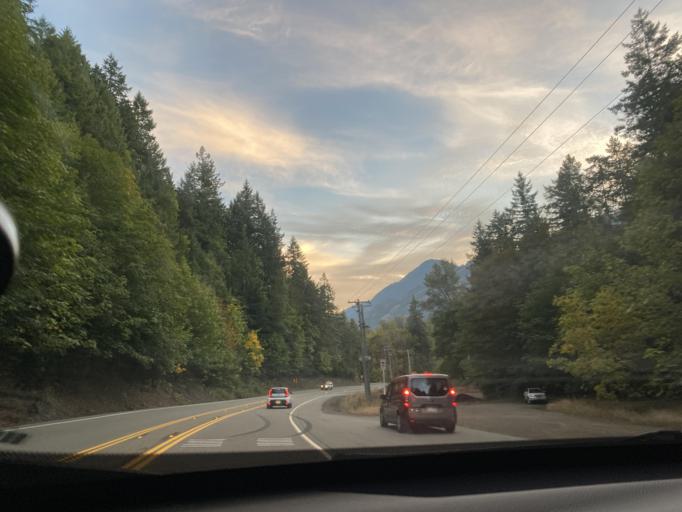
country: US
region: Washington
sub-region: Clallam County
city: Port Angeles
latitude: 48.0670
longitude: -123.5756
